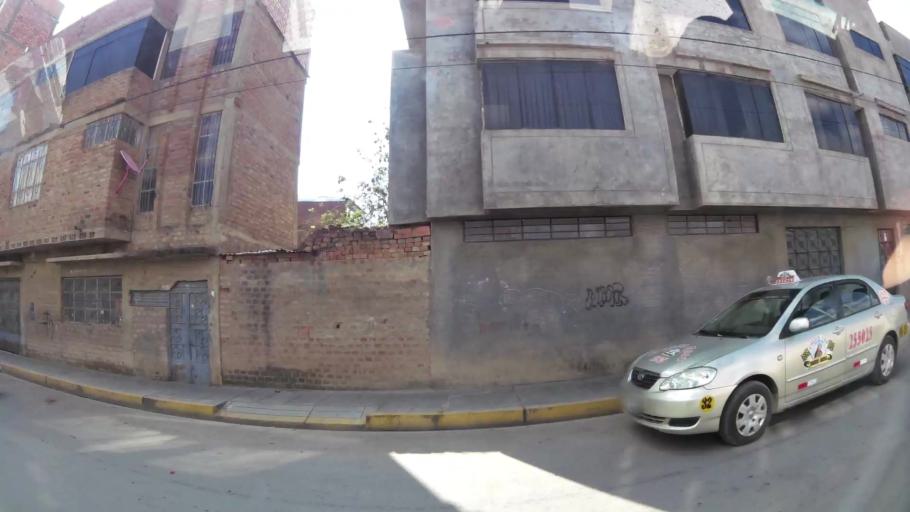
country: PE
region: Junin
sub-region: Provincia de Huancayo
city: El Tambo
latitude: -12.0780
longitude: -75.2126
